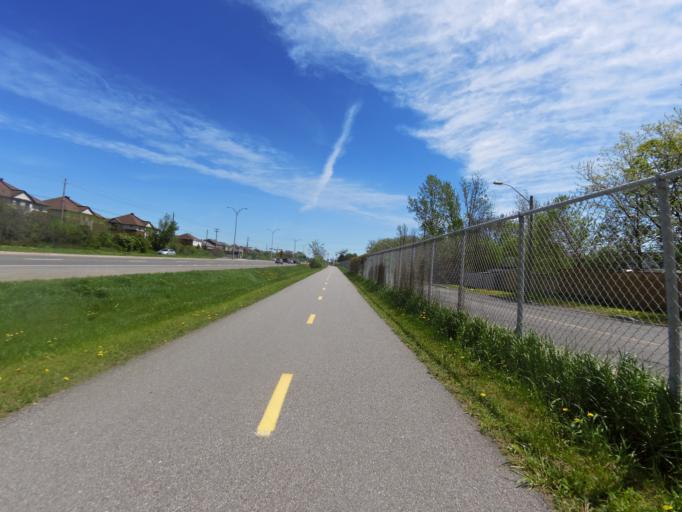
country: CA
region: Ontario
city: Bells Corners
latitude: 45.4093
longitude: -75.8518
